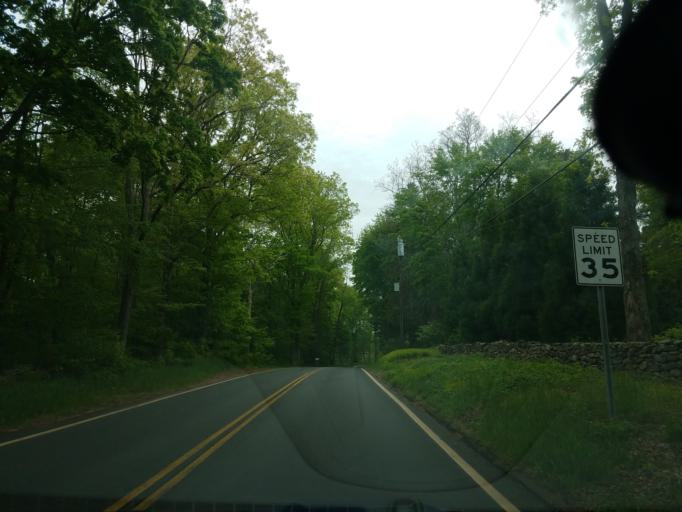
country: US
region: Connecticut
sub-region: Middlesex County
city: Durham
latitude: 41.4099
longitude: -72.6105
